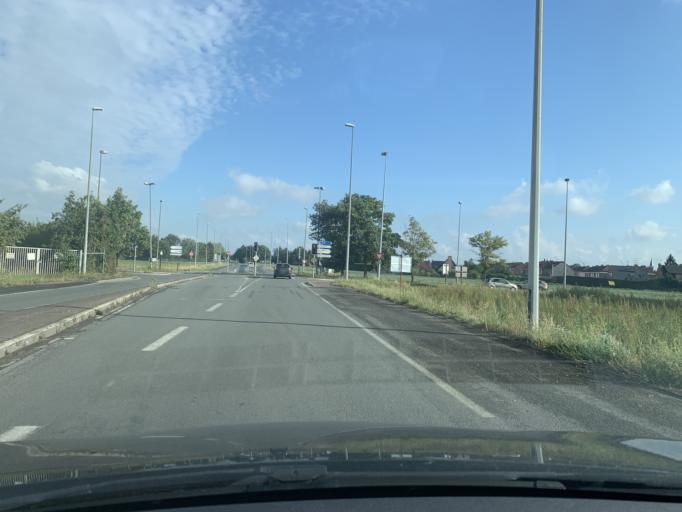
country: FR
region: Nord-Pas-de-Calais
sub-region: Departement du Nord
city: Emmerin
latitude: 50.5993
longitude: 3.0026
